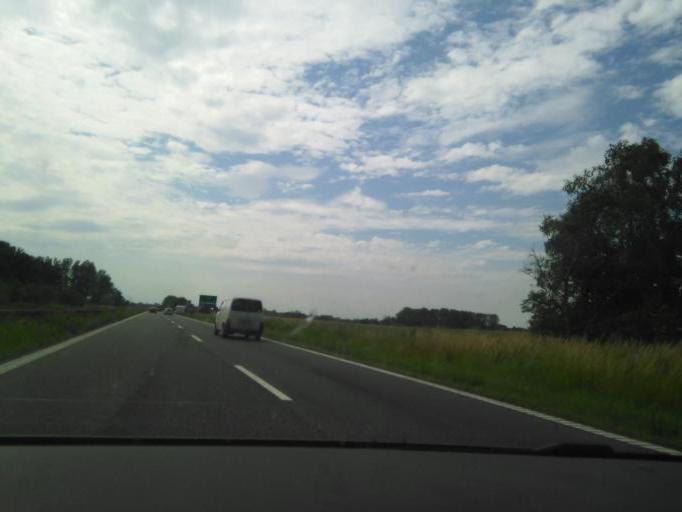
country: DK
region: Zealand
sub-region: Slagelse Kommune
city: Forlev
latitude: 55.3650
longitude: 11.2556
